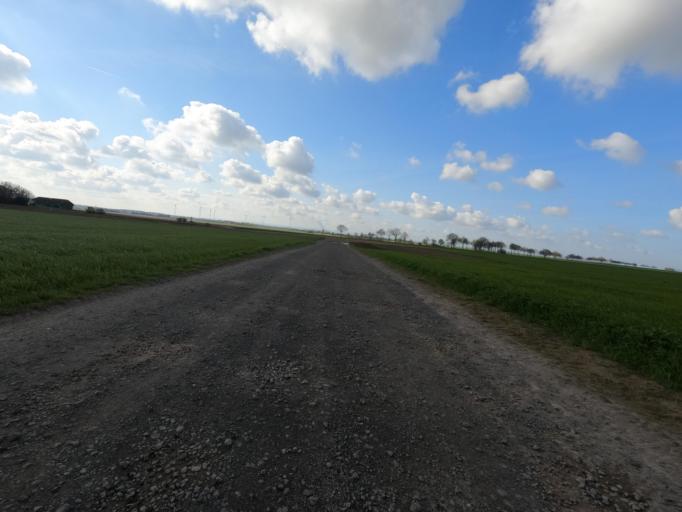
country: DE
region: North Rhine-Westphalia
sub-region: Regierungsbezirk Koln
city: Linnich
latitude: 50.9986
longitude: 6.3398
